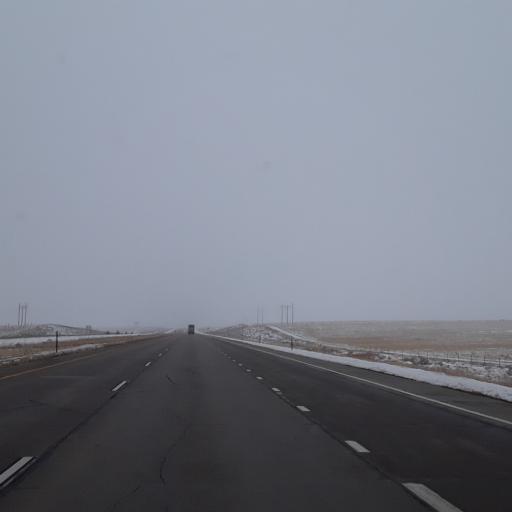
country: US
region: Colorado
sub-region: Logan County
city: Sterling
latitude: 40.7101
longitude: -103.0524
